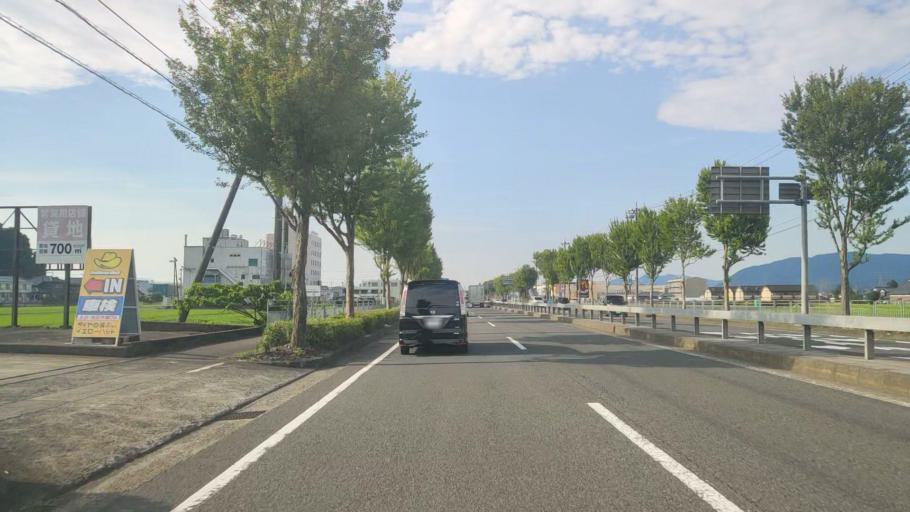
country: JP
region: Fukui
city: Takefu
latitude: 35.9029
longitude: 136.1922
